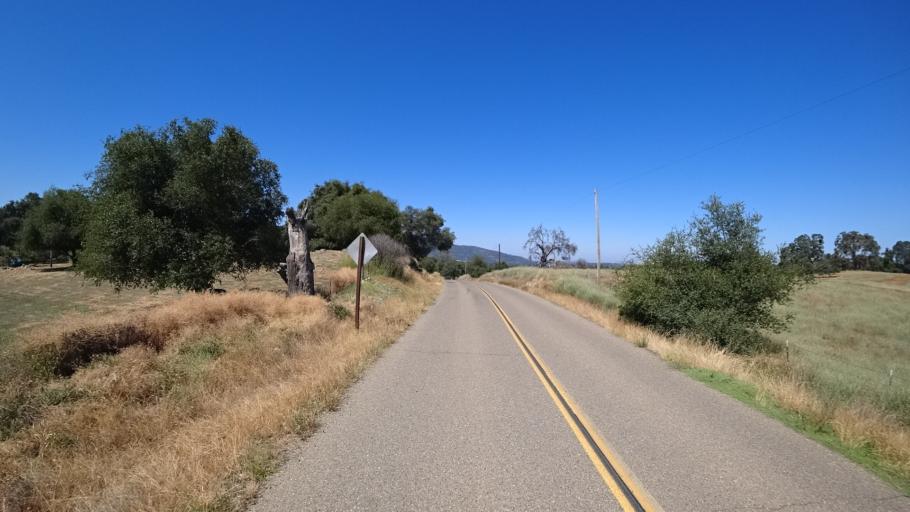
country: US
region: California
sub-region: Calaveras County
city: San Andreas
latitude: 38.1976
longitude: -120.6587
